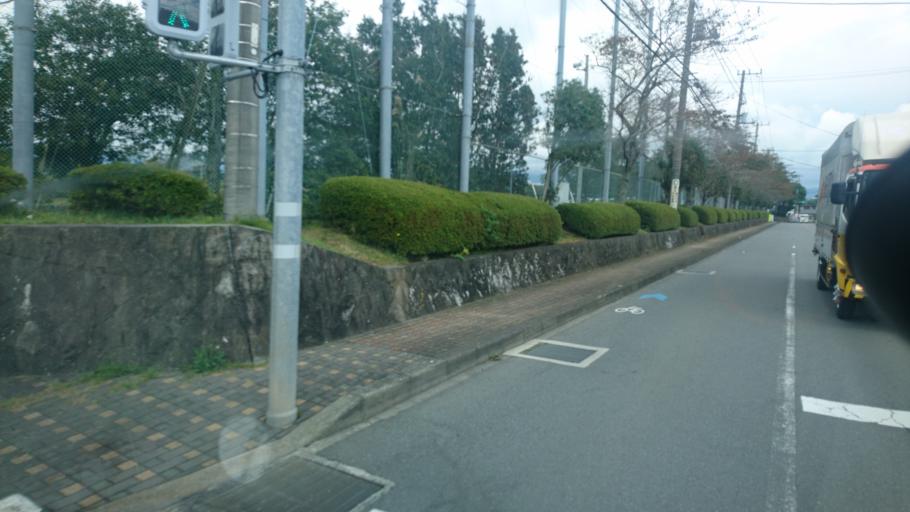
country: JP
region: Shizuoka
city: Gotemba
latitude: 35.3145
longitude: 138.9060
